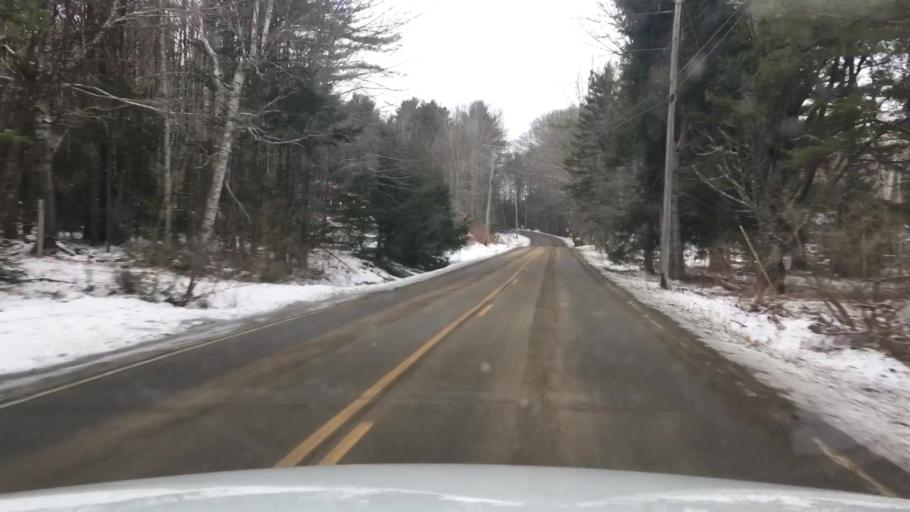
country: US
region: Maine
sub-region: Waldo County
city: Lincolnville
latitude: 44.2850
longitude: -69.0154
